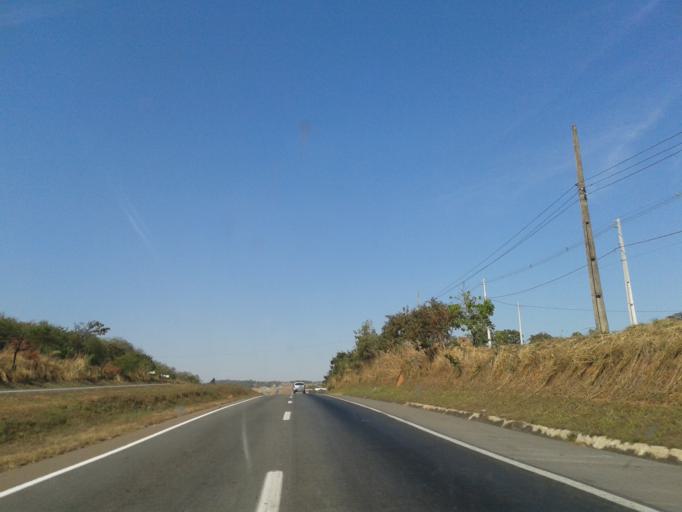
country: BR
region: Goias
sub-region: Aparecida De Goiania
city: Aparecida de Goiania
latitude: -16.8634
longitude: -49.2498
